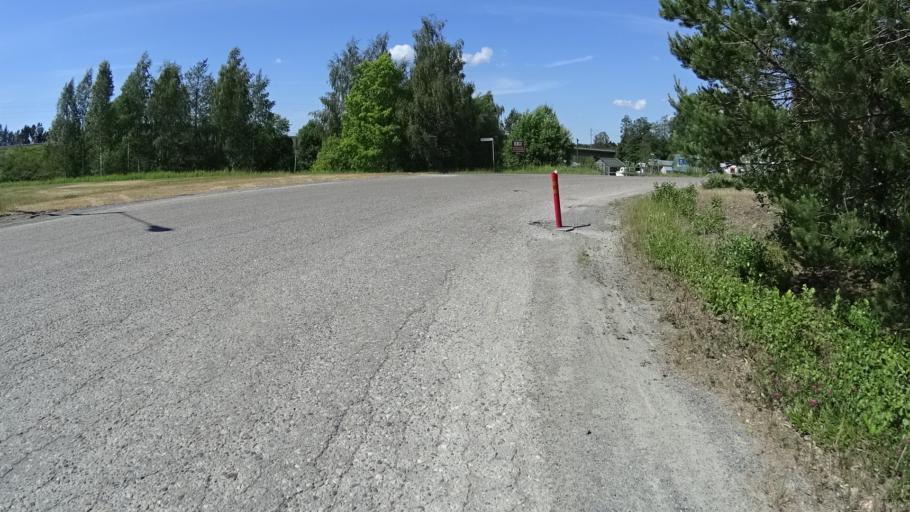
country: FI
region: Uusimaa
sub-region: Raaseporin
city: Pohja
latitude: 60.0918
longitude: 23.5661
